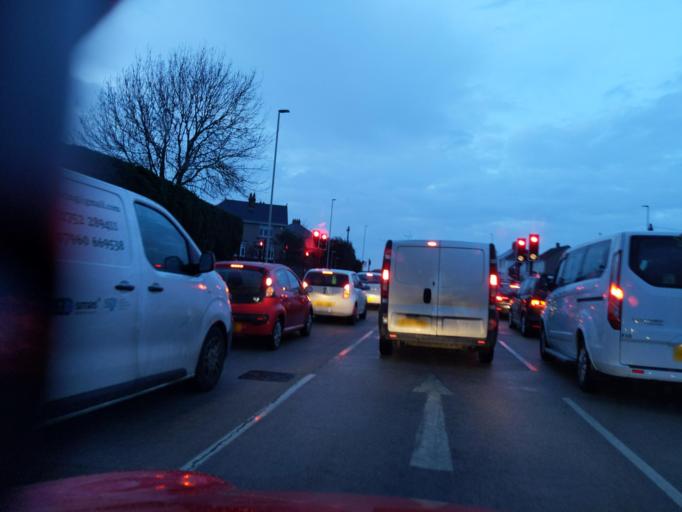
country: GB
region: England
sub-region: Plymouth
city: Plymstock
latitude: 50.3611
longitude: -4.0655
